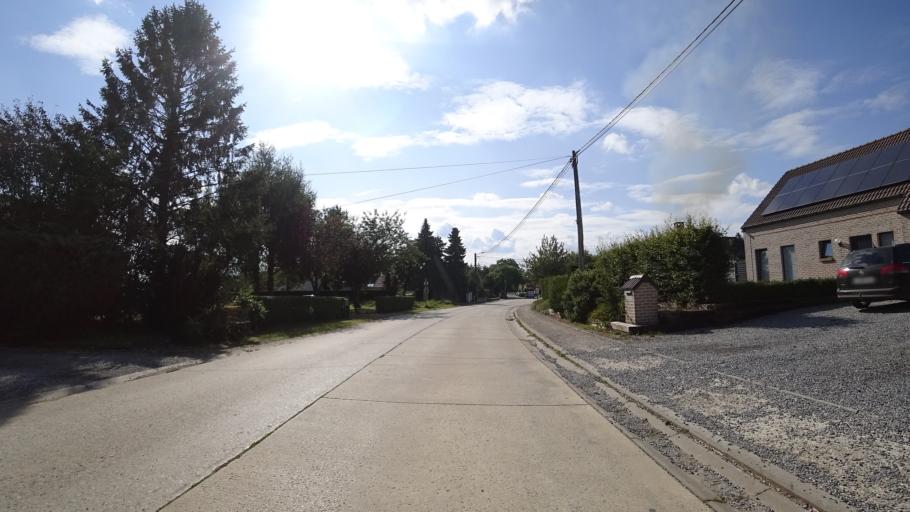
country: BE
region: Wallonia
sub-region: Province de Namur
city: Gembloux
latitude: 50.5195
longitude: 4.7022
